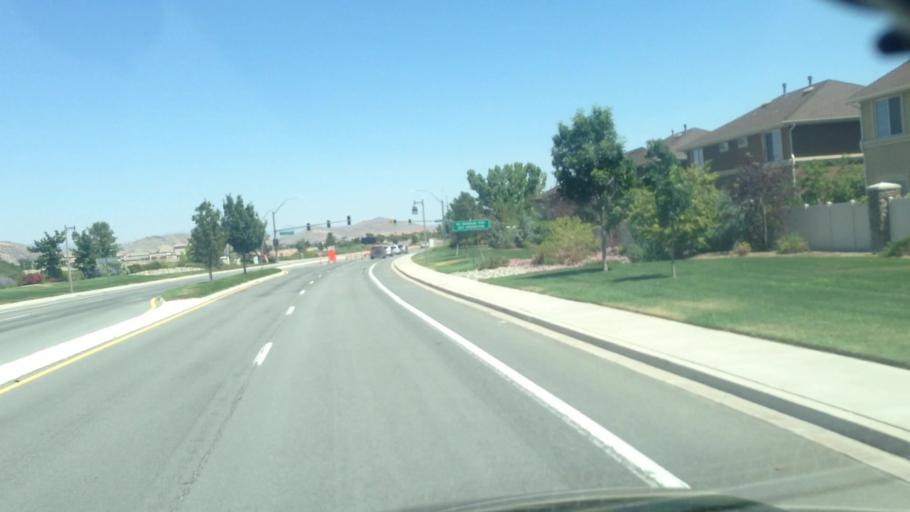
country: US
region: Nevada
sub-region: Washoe County
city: Sparks
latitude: 39.4148
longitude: -119.7333
